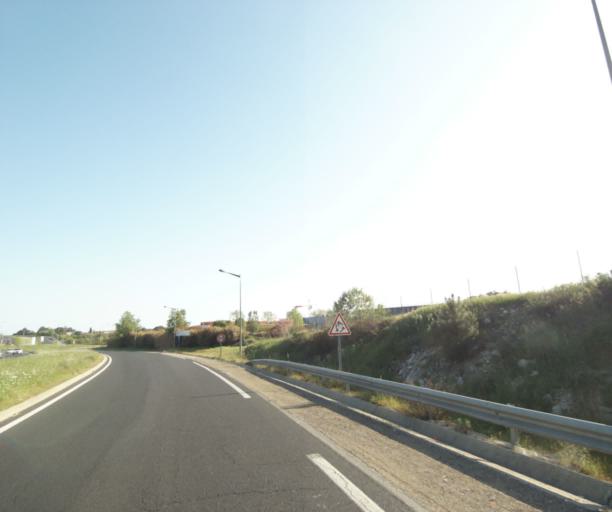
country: FR
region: Languedoc-Roussillon
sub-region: Departement de l'Herault
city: Le Cres
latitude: 43.6401
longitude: 3.9303
